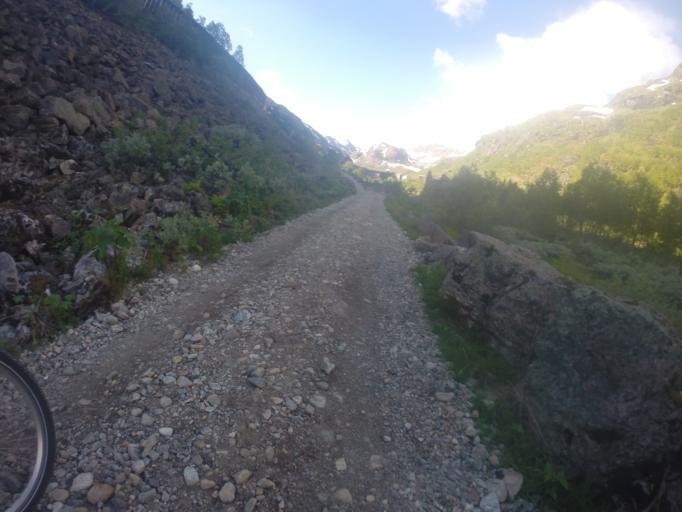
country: NO
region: Sogn og Fjordane
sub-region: Aurland
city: Aurlandsvangen
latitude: 60.7385
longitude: 7.1208
